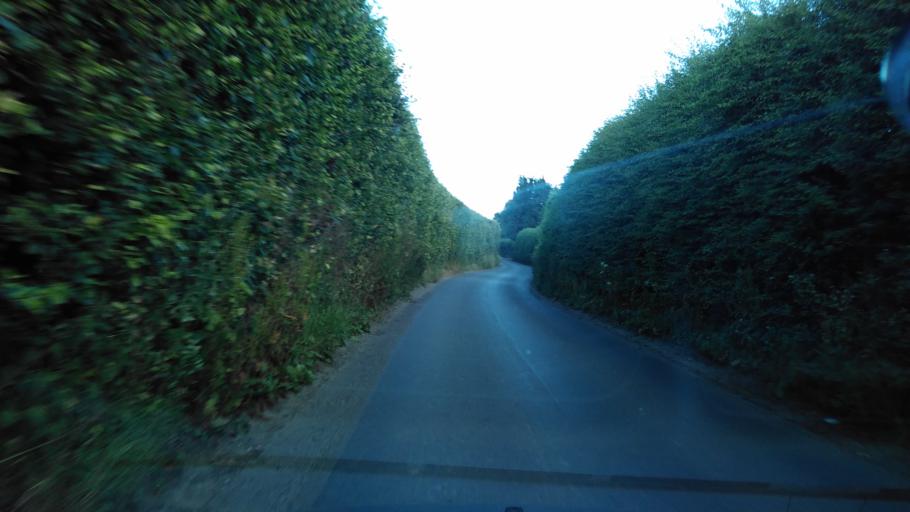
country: GB
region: England
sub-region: Kent
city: Dunkirk
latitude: 51.2707
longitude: 0.9436
